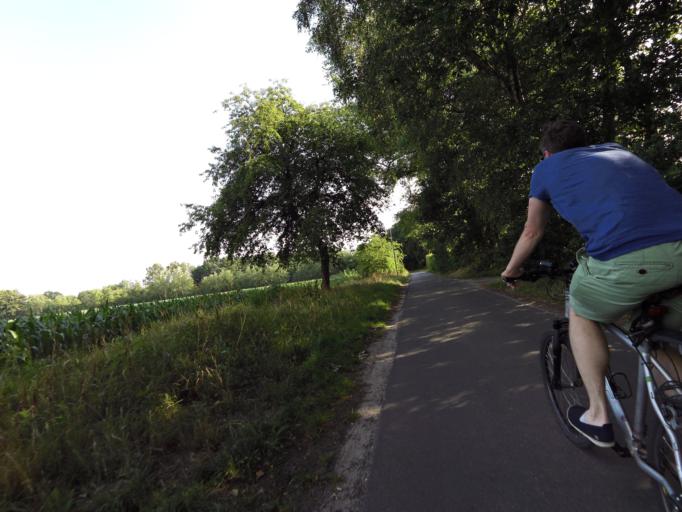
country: DE
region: Lower Saxony
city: Nordholz
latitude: 53.8382
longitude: 8.5848
